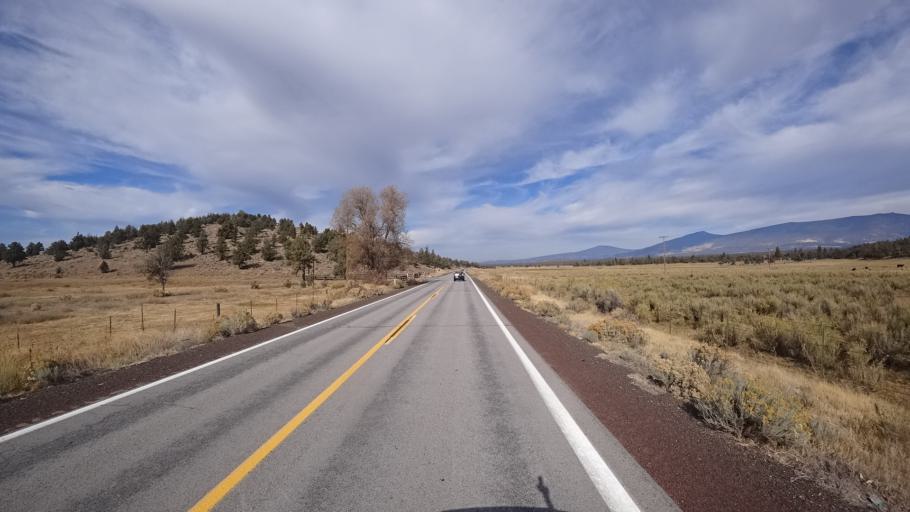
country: US
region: California
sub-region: Siskiyou County
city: Weed
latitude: 41.5592
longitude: -122.3873
